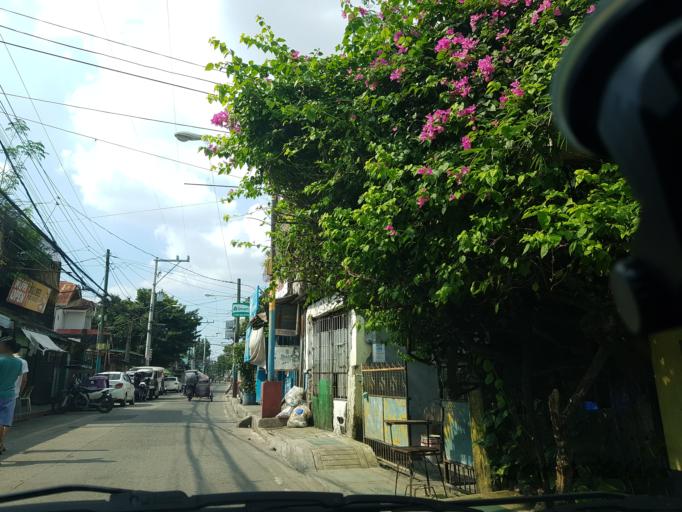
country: PH
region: Calabarzon
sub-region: Province of Rizal
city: Pateros
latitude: 14.5580
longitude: 121.0903
